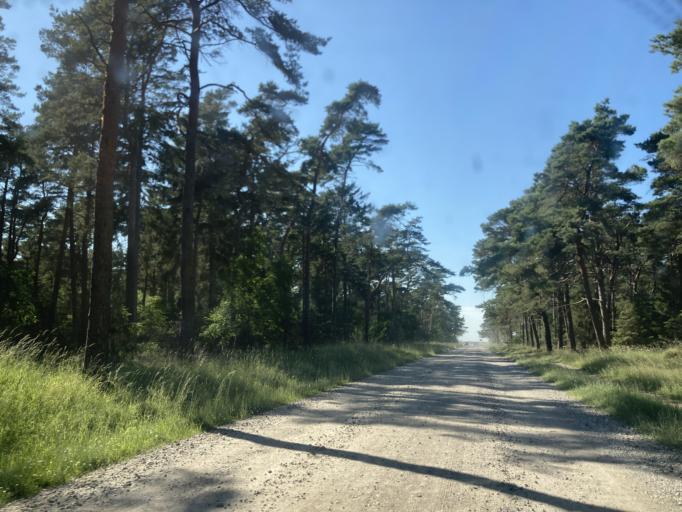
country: DK
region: Capital Region
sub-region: Halsnaes Kommune
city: Frederiksvaerk
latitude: 56.0200
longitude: 12.0062
